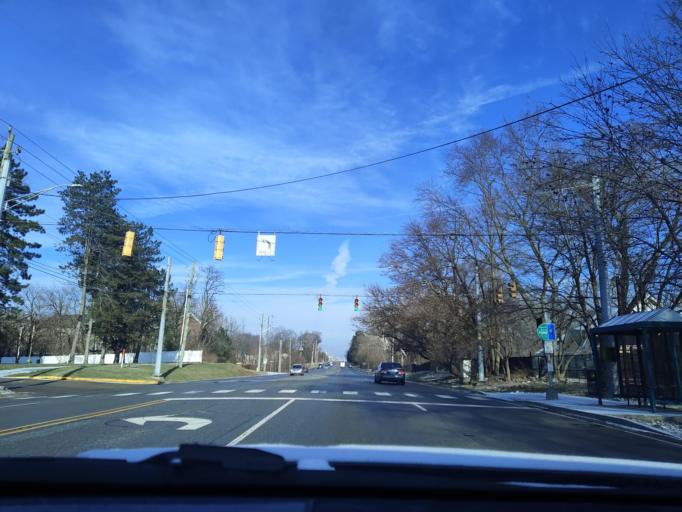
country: US
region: Indiana
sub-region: Marion County
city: Meridian Hills
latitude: 39.8993
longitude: -86.2167
